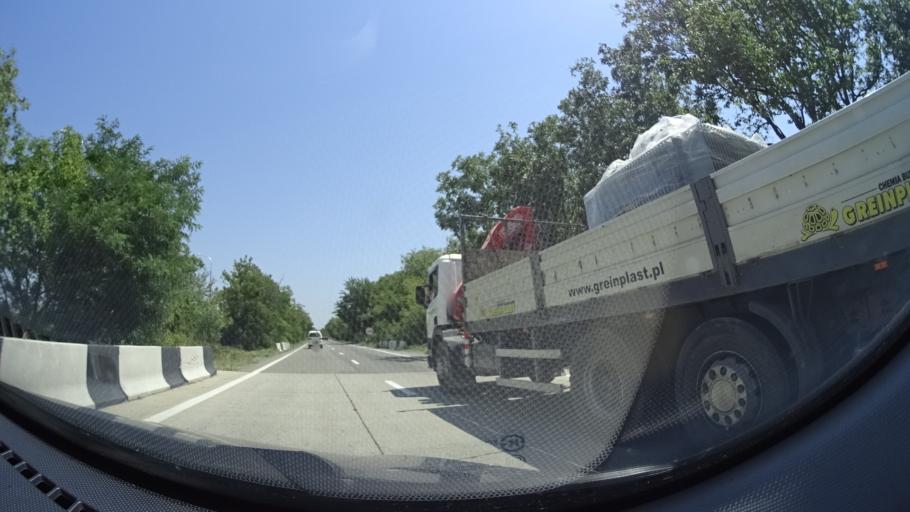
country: GE
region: Shida Kartli
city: Kaspi
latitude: 41.9644
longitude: 44.4698
